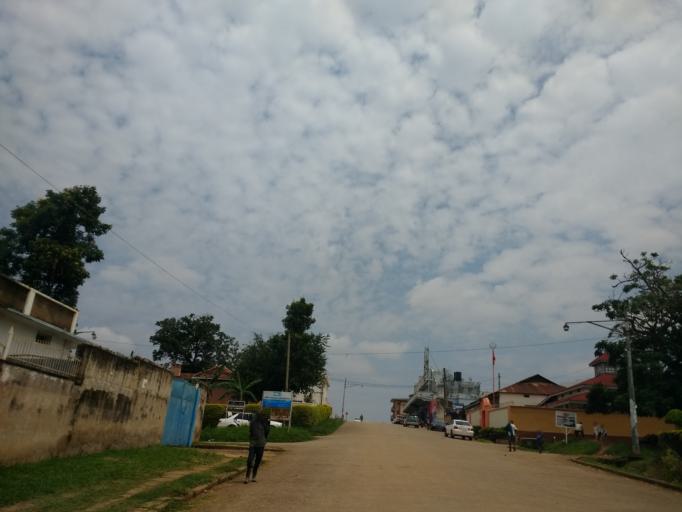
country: UG
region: Eastern Region
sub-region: Mbale District
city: Mbale
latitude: 1.0736
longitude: 34.1810
